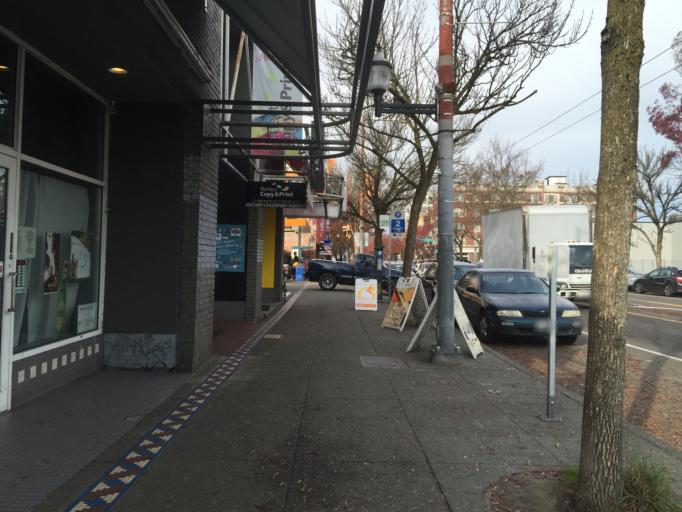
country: US
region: Washington
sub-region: King County
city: Seattle
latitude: 47.6190
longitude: -122.3211
